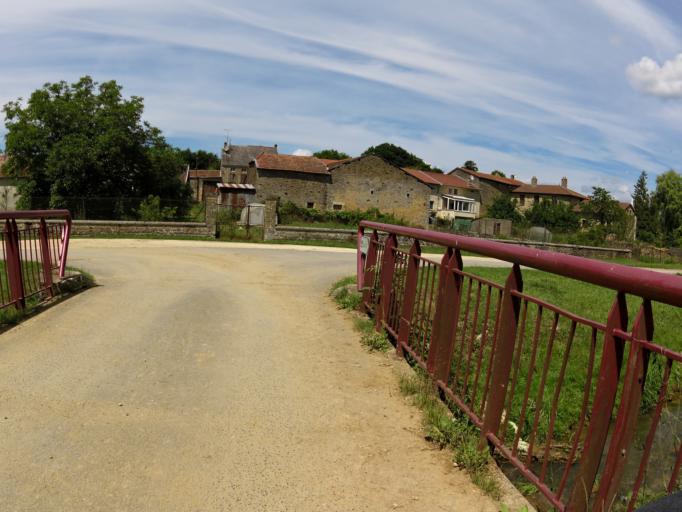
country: FR
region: Champagne-Ardenne
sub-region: Departement des Ardennes
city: Mouzon
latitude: 49.5442
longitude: 5.0826
